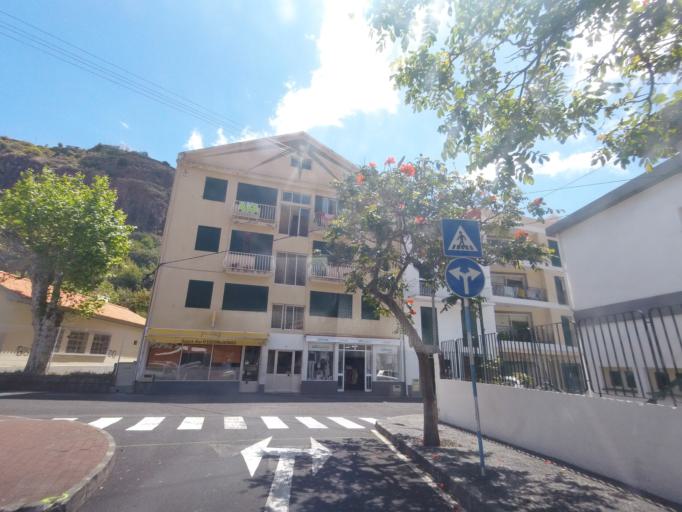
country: PT
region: Madeira
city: Ribeira Brava
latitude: 32.6730
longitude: -17.0640
